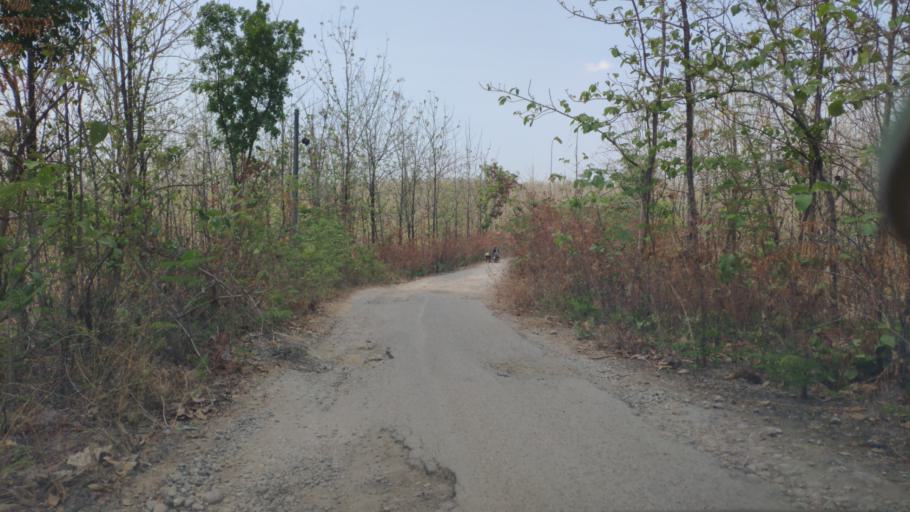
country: ID
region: Central Java
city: Randublatung
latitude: -7.2469
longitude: 111.3790
